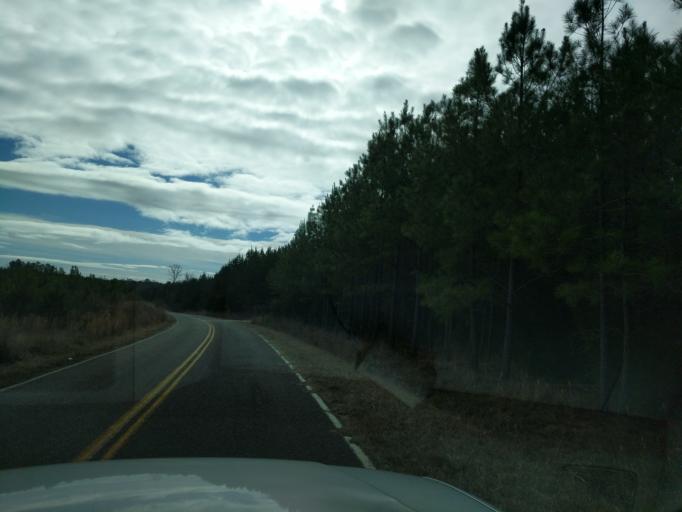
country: US
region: South Carolina
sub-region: Edgefield County
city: Edgefield
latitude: 33.9189
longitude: -82.0070
